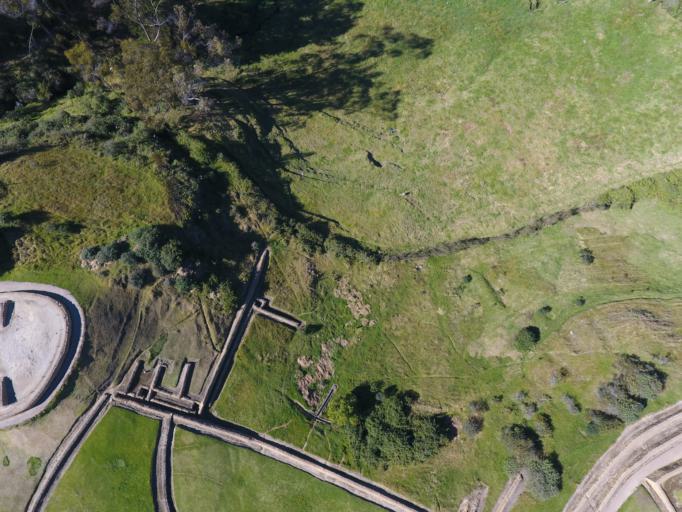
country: EC
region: Canar
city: Canar
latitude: -2.5407
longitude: -78.8743
